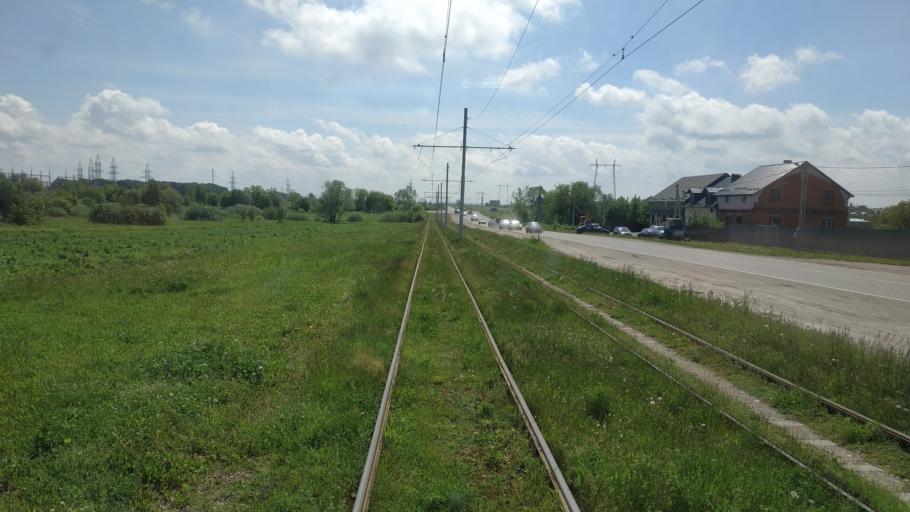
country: RU
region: Moskovskaya
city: Sychevo
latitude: 55.0621
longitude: 38.7261
